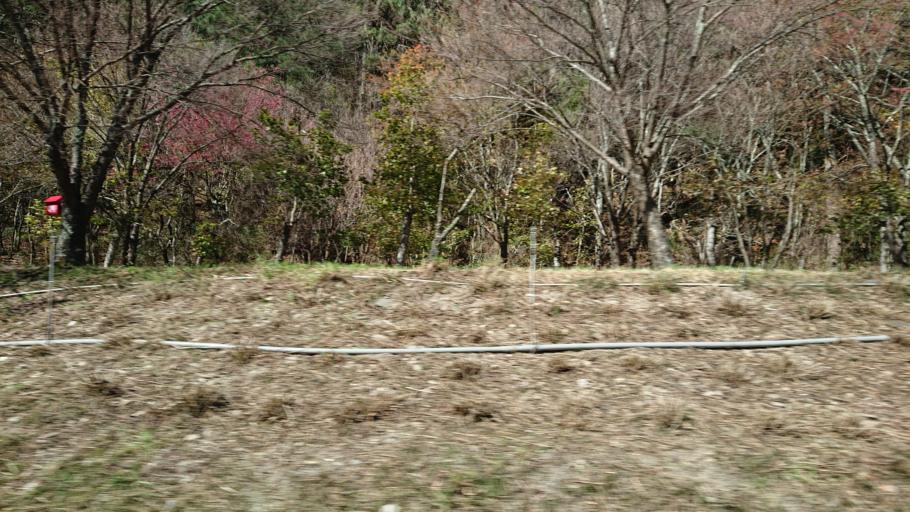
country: TW
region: Taiwan
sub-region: Hualien
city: Hualian
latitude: 24.3496
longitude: 121.3080
